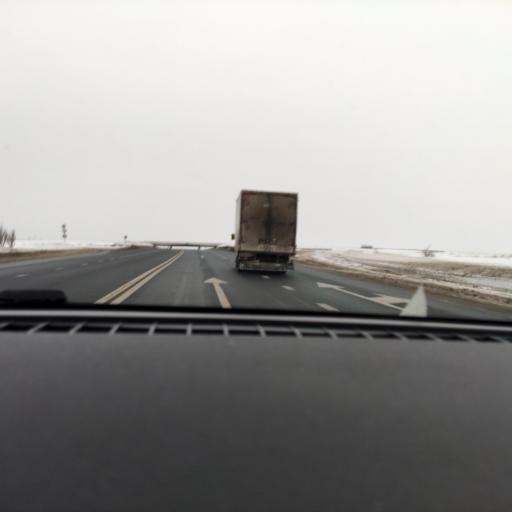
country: RU
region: Samara
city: Petra-Dubrava
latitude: 53.3354
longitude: 50.4529
